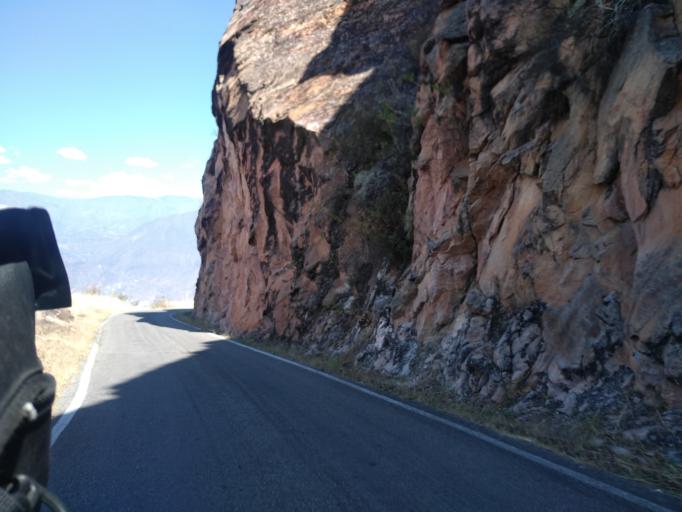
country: PE
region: Amazonas
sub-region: Provincia de Chachapoyas
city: Balsas
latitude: -6.8495
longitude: -77.9825
